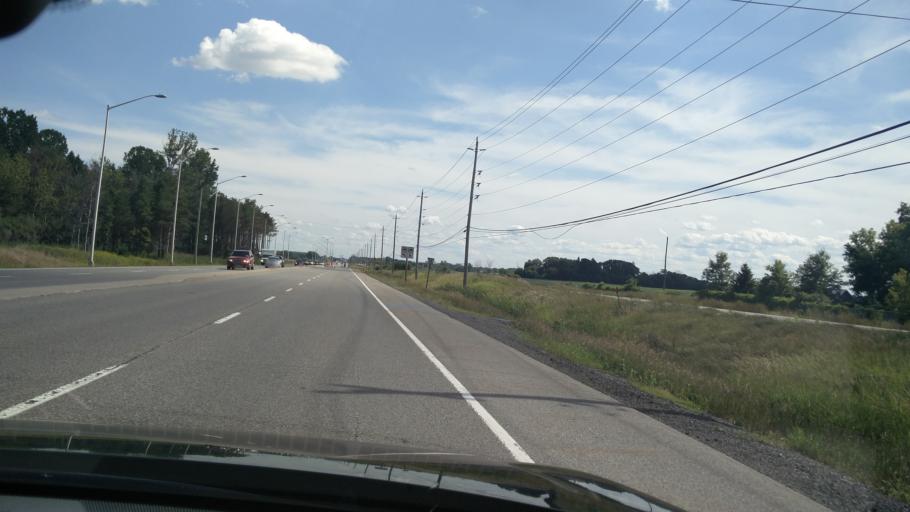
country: CA
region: Ontario
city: Bells Corners
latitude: 45.3133
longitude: -75.7398
